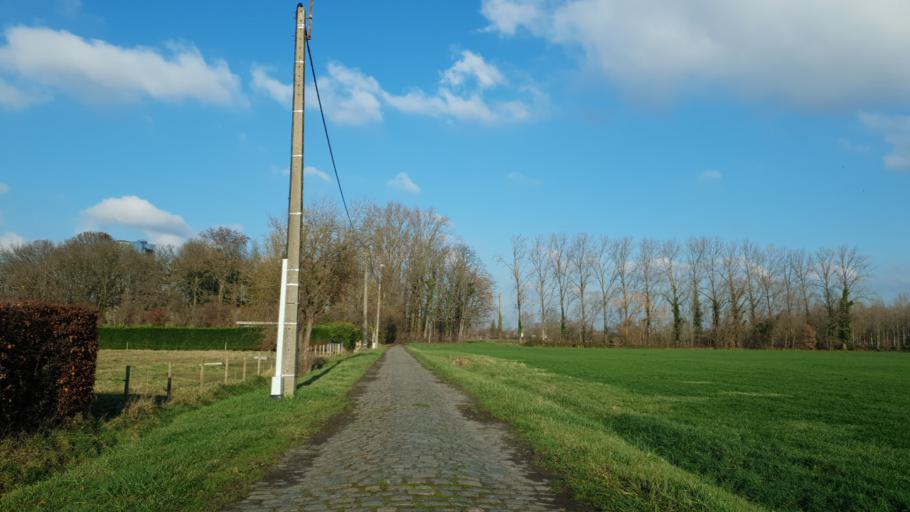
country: BE
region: Flanders
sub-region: Provincie Vlaams-Brabant
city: Herent
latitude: 50.9248
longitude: 4.6809
